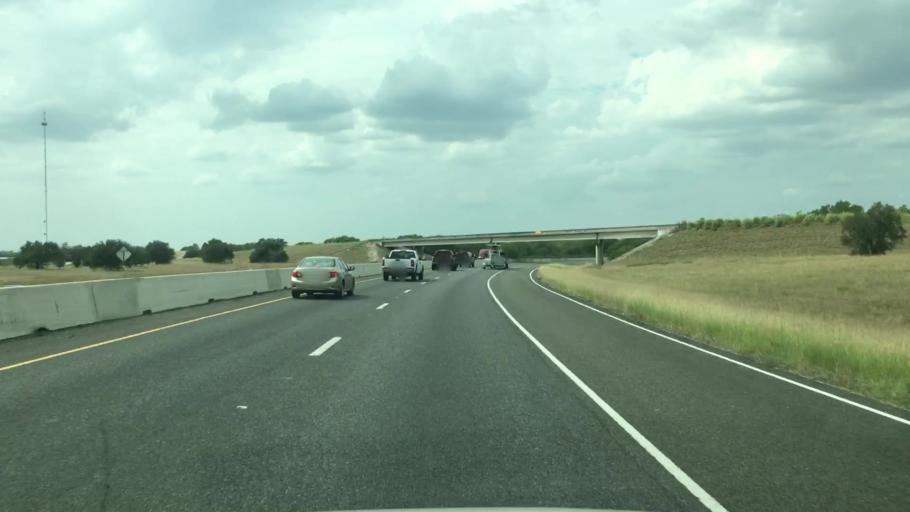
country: US
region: Texas
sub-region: Atascosa County
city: Pleasanton
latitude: 28.9081
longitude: -98.4324
